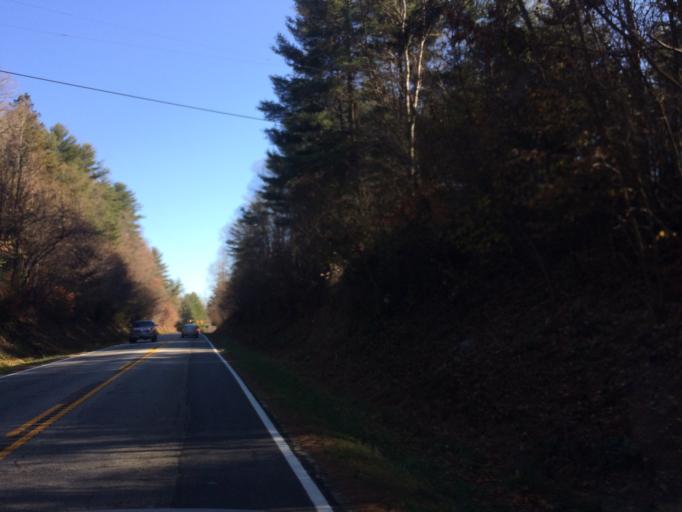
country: US
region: North Carolina
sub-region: Henderson County
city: Mountain Home
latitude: 35.3691
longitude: -82.5269
